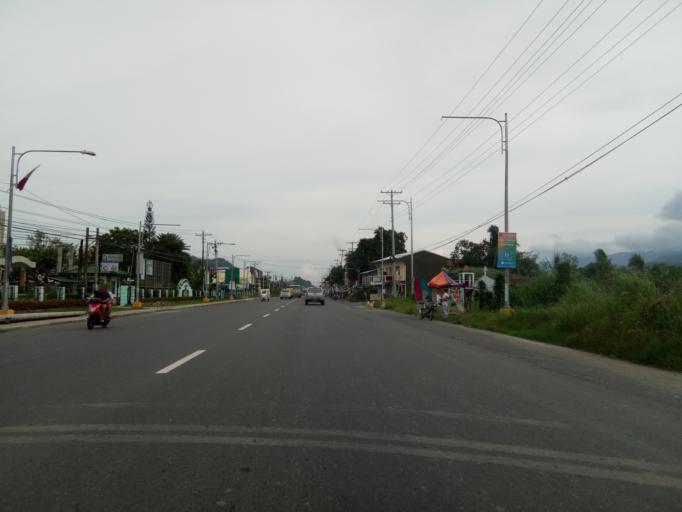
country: PH
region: Caraga
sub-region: Province of Surigao del Norte
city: Rizal
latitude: 9.7672
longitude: 125.4833
